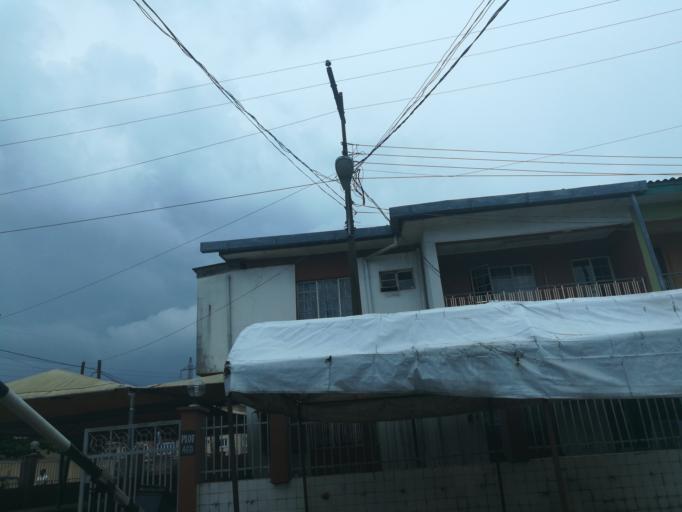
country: NG
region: Lagos
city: Agege
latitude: 6.6203
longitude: 3.3457
